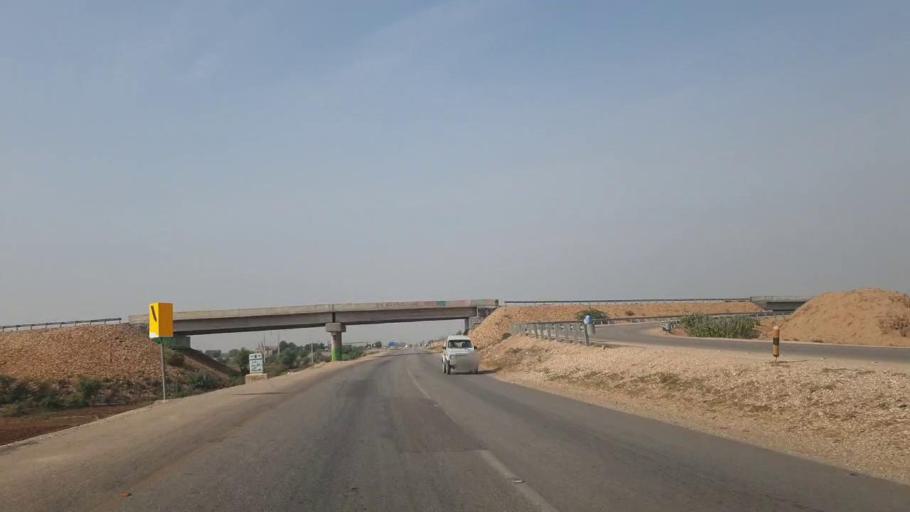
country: PK
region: Sindh
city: Sann
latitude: 26.1548
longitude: 68.0242
